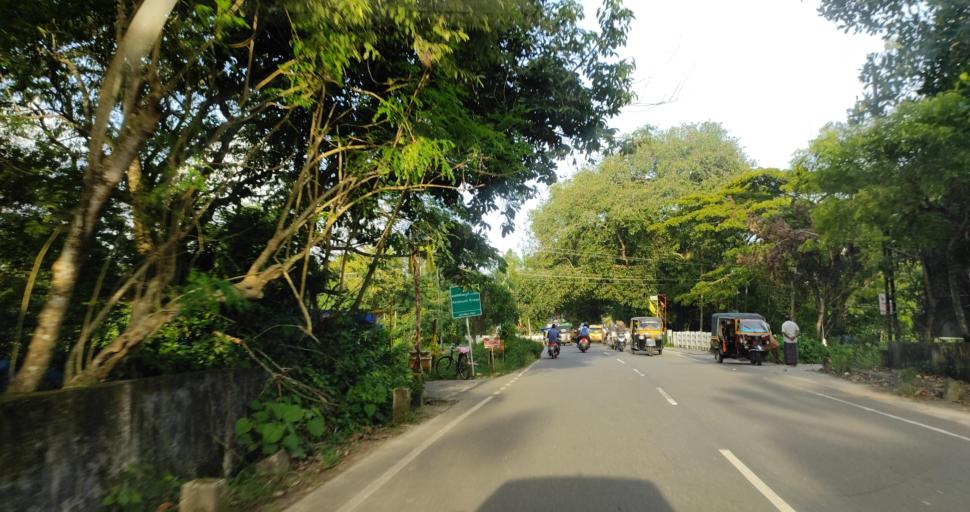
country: IN
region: Kerala
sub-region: Alappuzha
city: Shertallai
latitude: 9.6088
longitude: 76.3333
